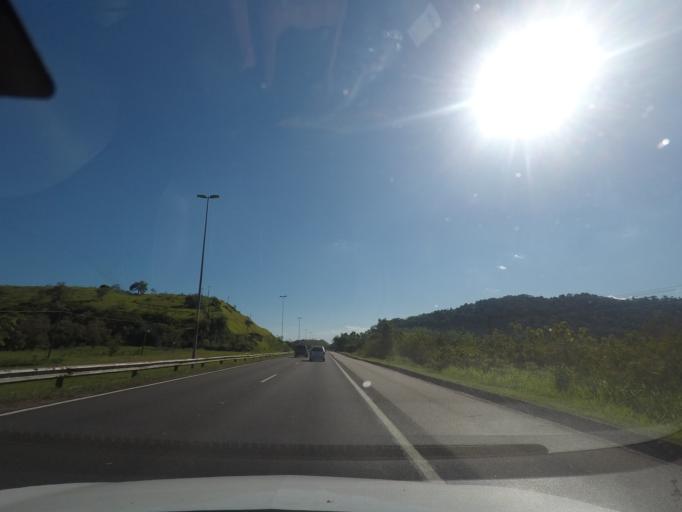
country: BR
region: Rio de Janeiro
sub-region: Guapimirim
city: Guapimirim
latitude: -22.6293
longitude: -43.0501
